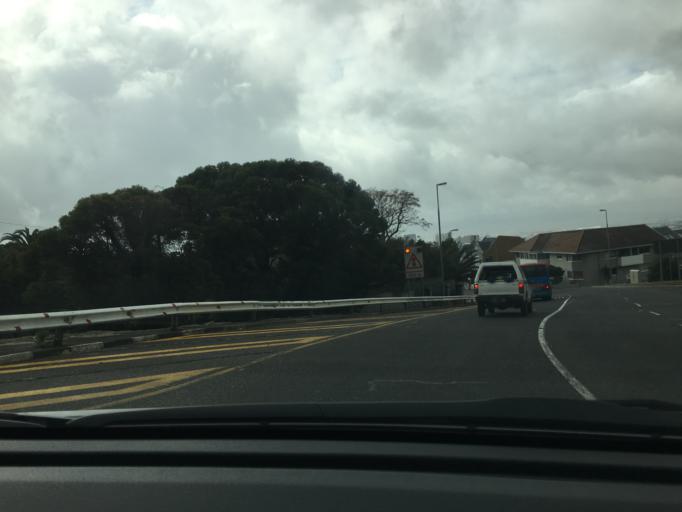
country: ZA
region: Western Cape
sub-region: City of Cape Town
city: Cape Town
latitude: -33.9345
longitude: 18.4025
